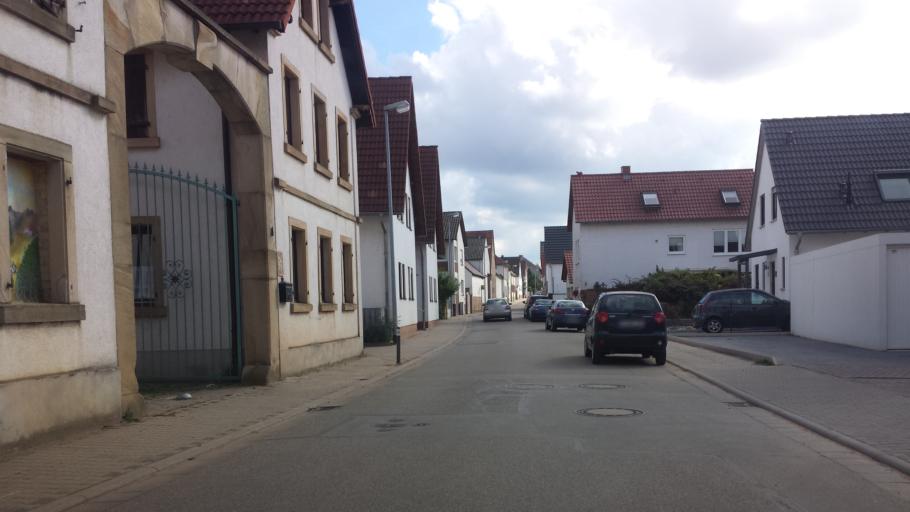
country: DE
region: Rheinland-Pfalz
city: Hochdorf-Assenheim
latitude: 49.4228
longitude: 8.2841
